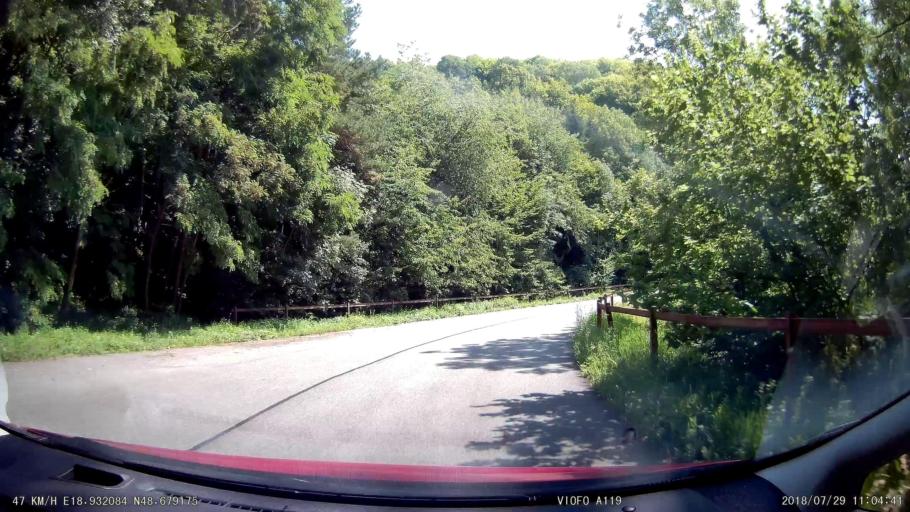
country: SK
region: Banskobystricky
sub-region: Okres Ziar nad Hronom
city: Kremnica
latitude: 48.6792
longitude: 18.9322
